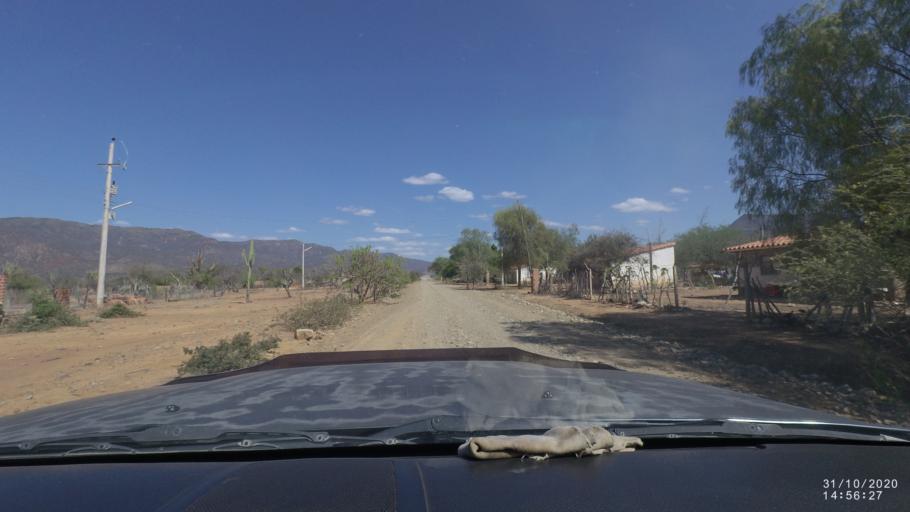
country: BO
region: Cochabamba
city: Aiquile
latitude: -18.2385
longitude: -64.8503
